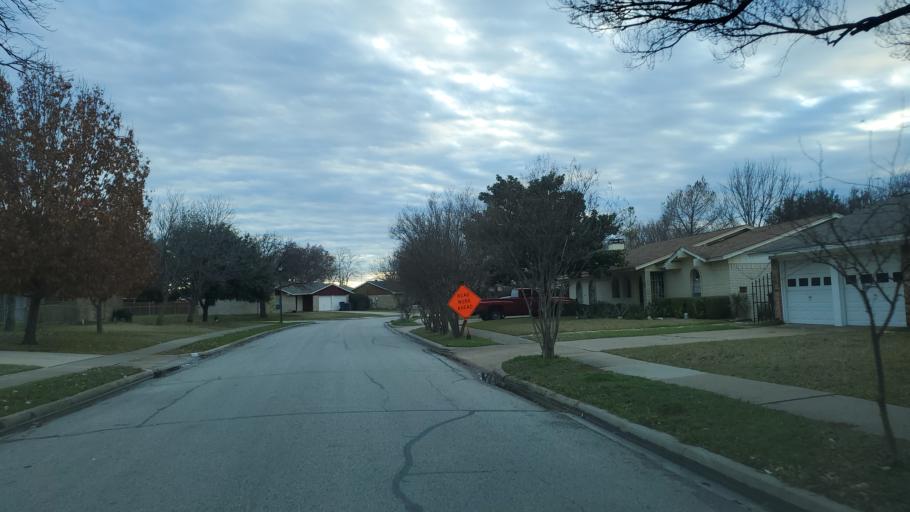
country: US
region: Texas
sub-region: Dallas County
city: Carrollton
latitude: 32.9876
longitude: -96.8854
